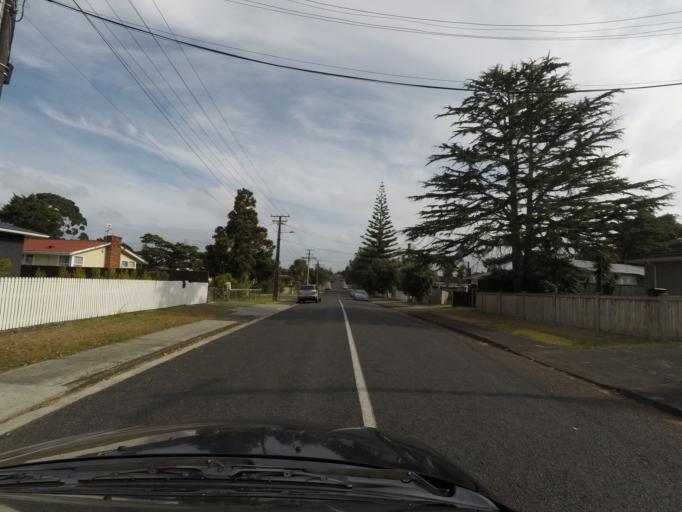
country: NZ
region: Auckland
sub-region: Auckland
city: Rosebank
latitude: -36.8912
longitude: 174.6681
